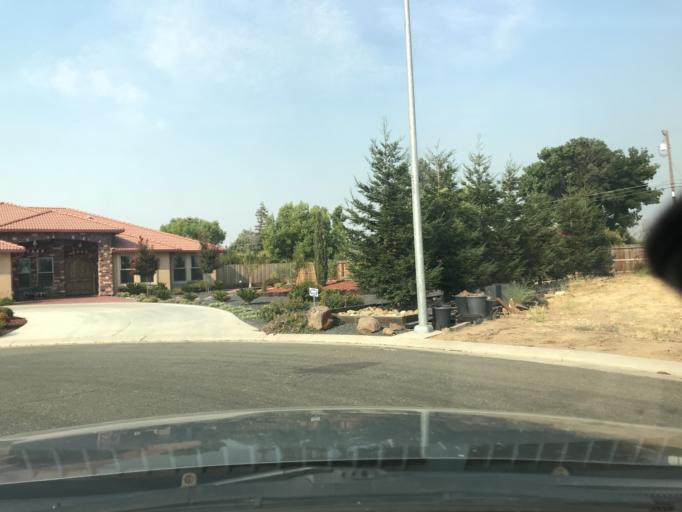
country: US
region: California
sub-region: Merced County
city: Atwater
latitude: 37.3175
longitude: -120.5970
